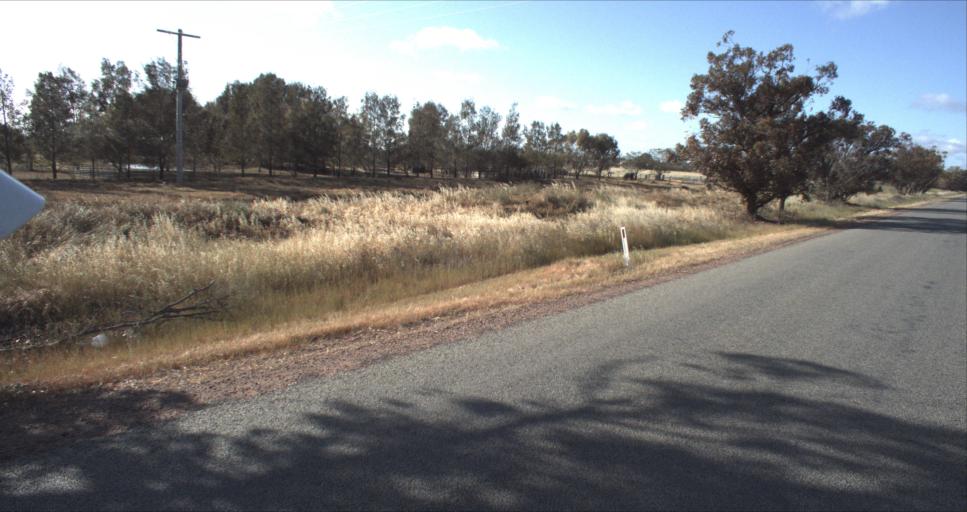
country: AU
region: New South Wales
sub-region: Leeton
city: Leeton
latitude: -34.5205
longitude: 146.3907
